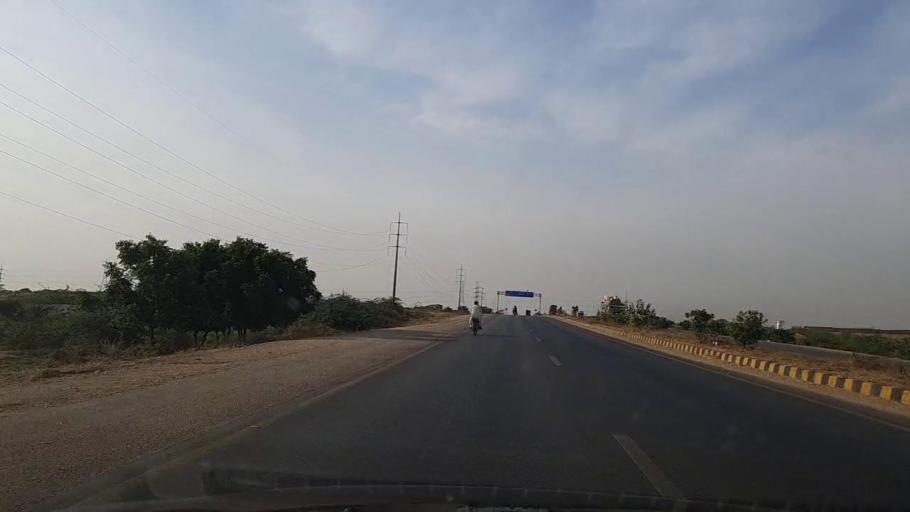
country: PK
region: Sindh
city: Gharo
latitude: 24.7636
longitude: 67.5545
